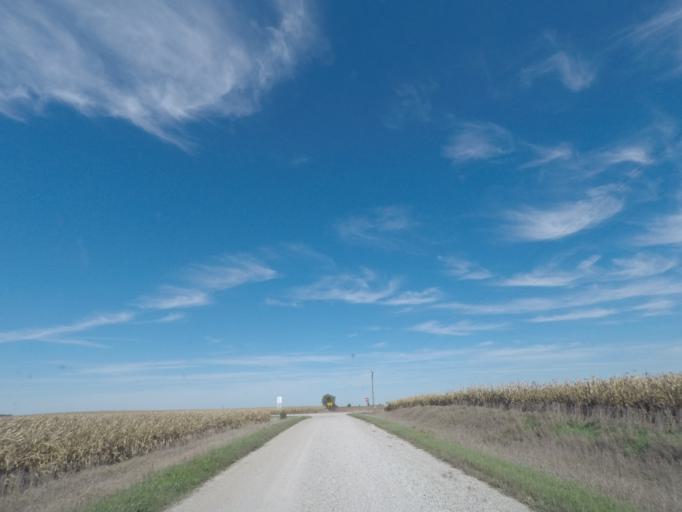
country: US
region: Iowa
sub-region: Story County
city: Nevada
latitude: 42.0218
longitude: -93.3573
